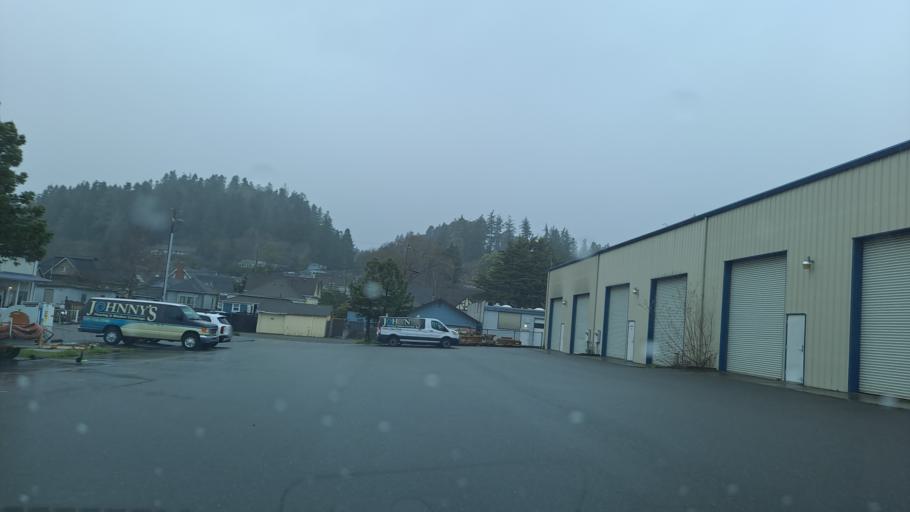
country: US
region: California
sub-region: Humboldt County
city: Fortuna
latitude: 40.5974
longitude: -124.1608
